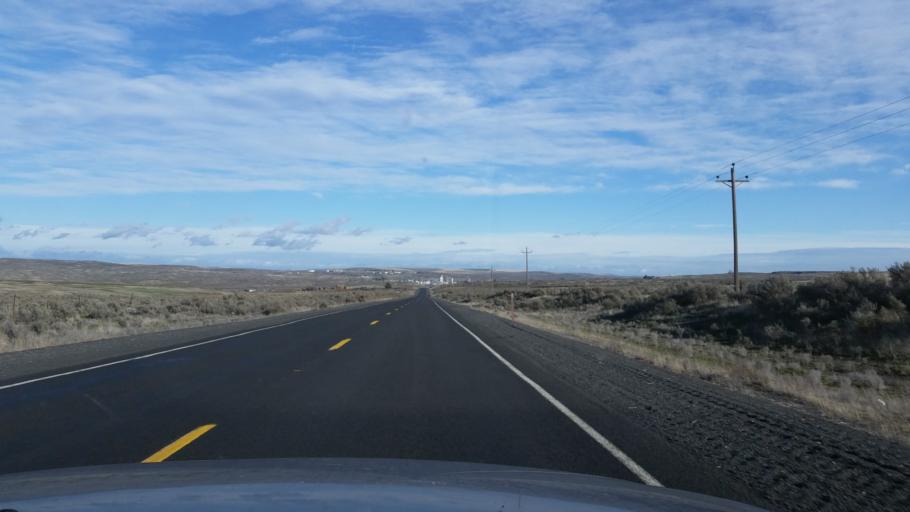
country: US
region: Washington
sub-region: Adams County
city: Ritzville
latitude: 47.3208
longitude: -118.7329
